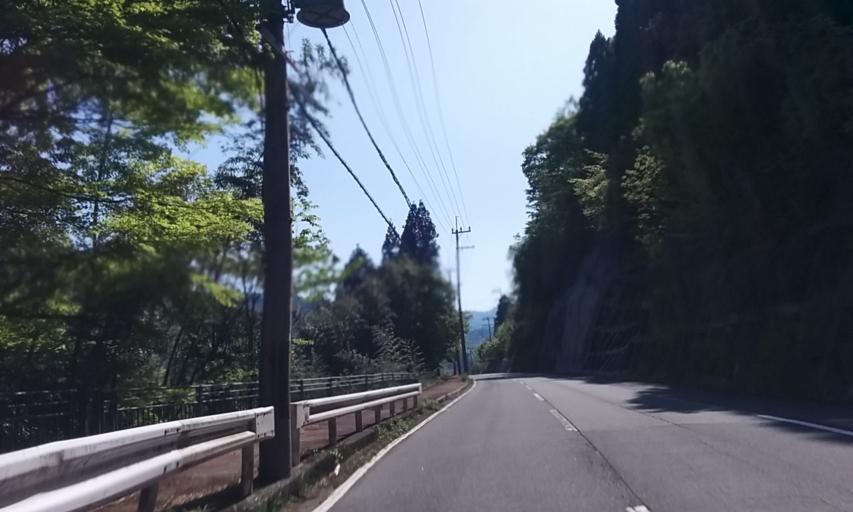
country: JP
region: Kyoto
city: Maizuru
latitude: 35.2793
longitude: 135.5226
